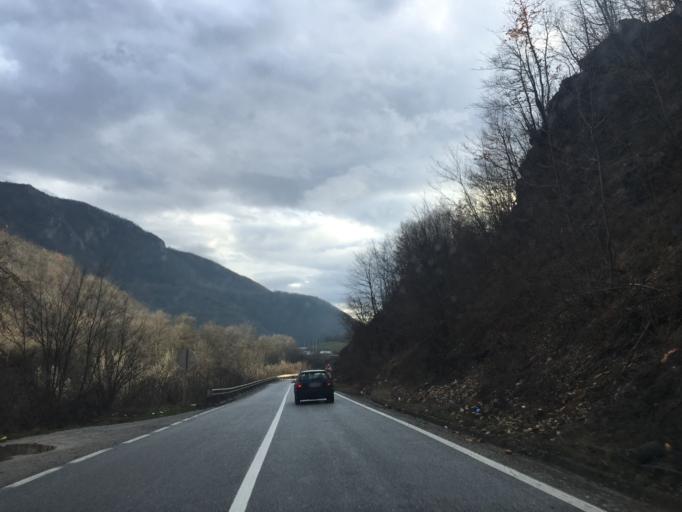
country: RS
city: Sokolovo Brdo
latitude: 43.1495
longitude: 19.7792
